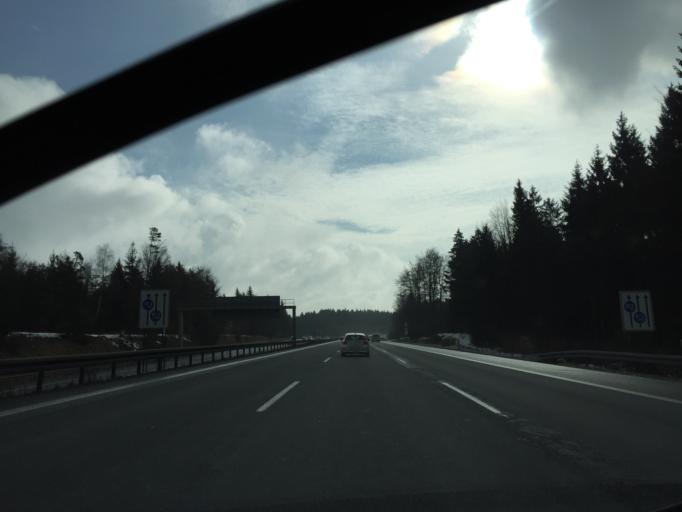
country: DE
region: Bavaria
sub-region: Upper Bavaria
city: Denkendorf
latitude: 48.9613
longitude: 11.4216
